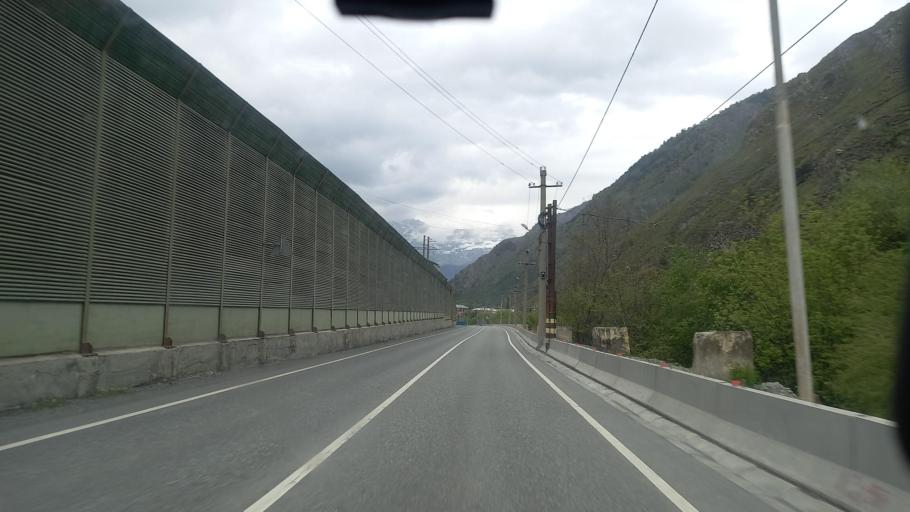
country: RU
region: North Ossetia
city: Mizur
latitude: 42.8518
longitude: 44.0646
